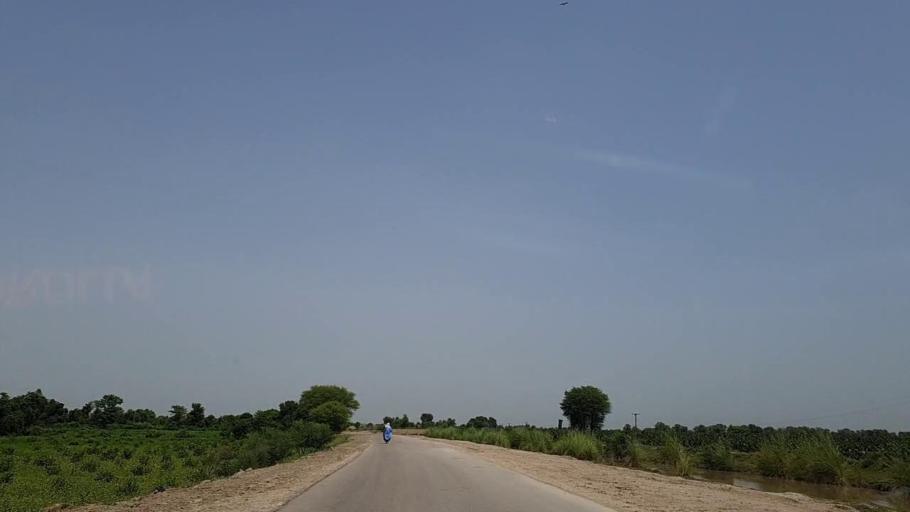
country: PK
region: Sindh
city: Tharu Shah
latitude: 26.8878
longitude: 68.0120
